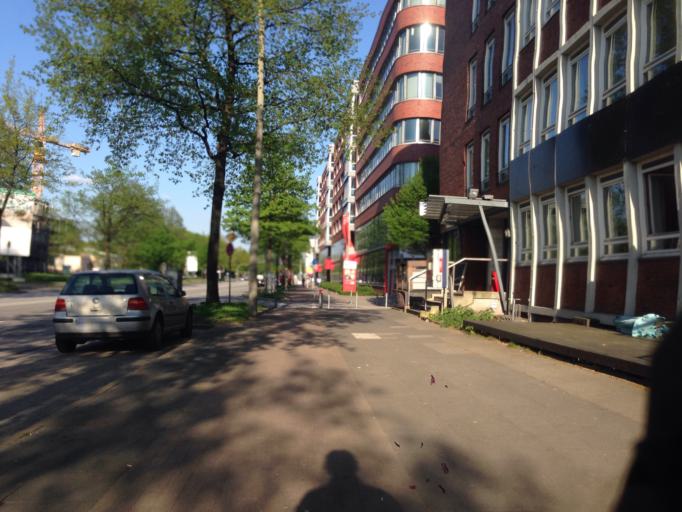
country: DE
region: Hamburg
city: Borgfelde
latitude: 53.5522
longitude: 10.0311
